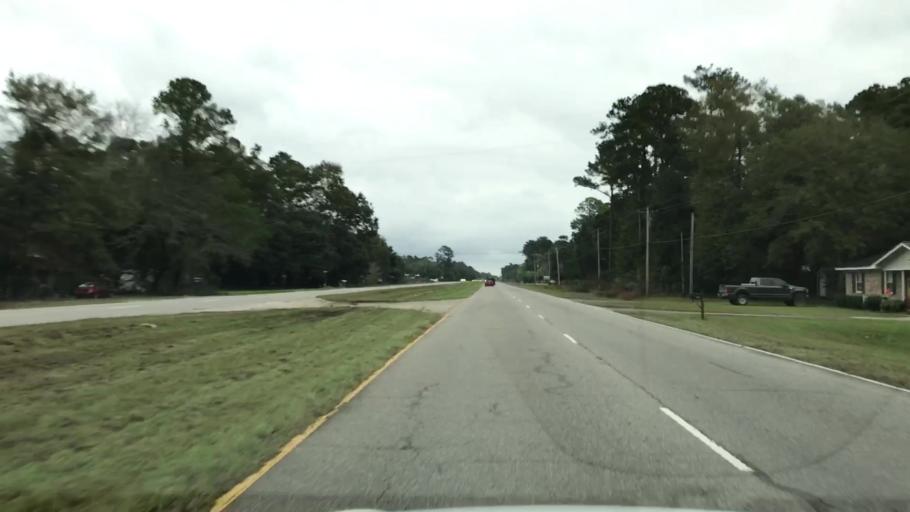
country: US
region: South Carolina
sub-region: Georgetown County
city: Georgetown
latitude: 33.3132
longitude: -79.3290
